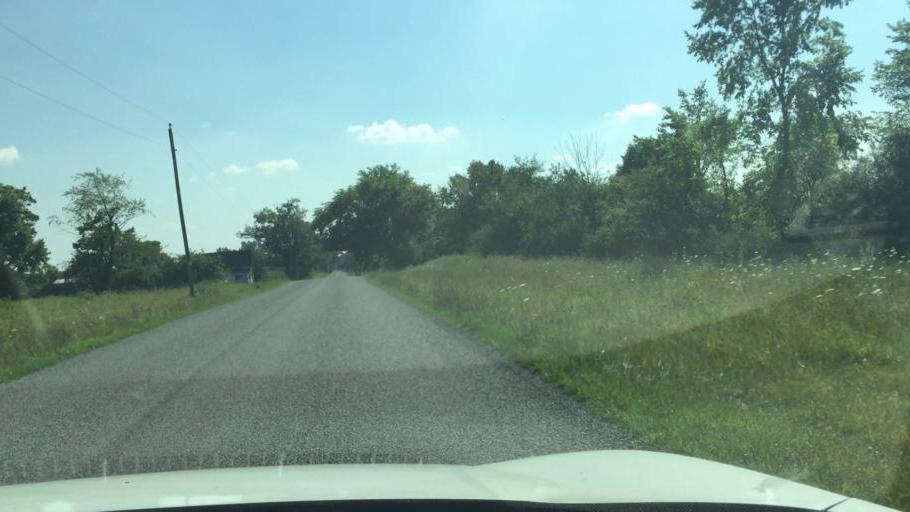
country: US
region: Ohio
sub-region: Champaign County
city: North Lewisburg
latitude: 40.2575
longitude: -83.5099
